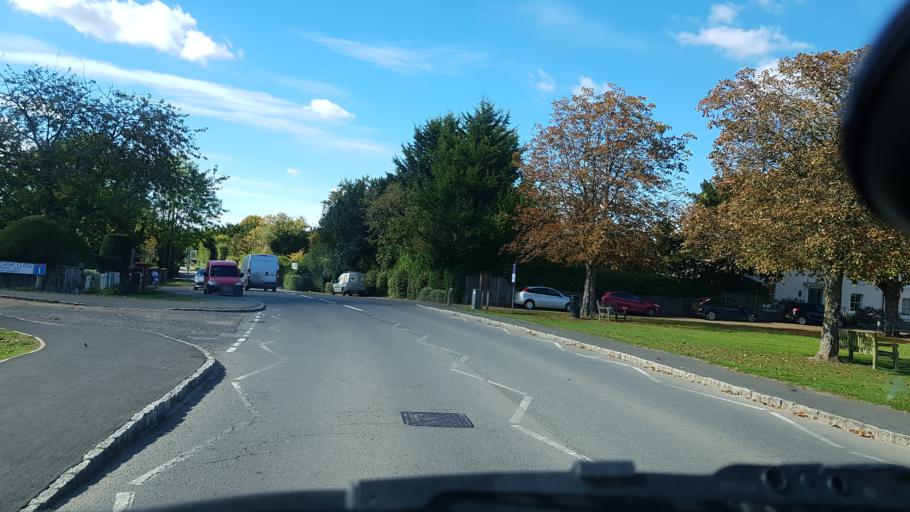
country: GB
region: England
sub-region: West Sussex
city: Billingshurst
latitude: 51.0231
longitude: -0.5052
